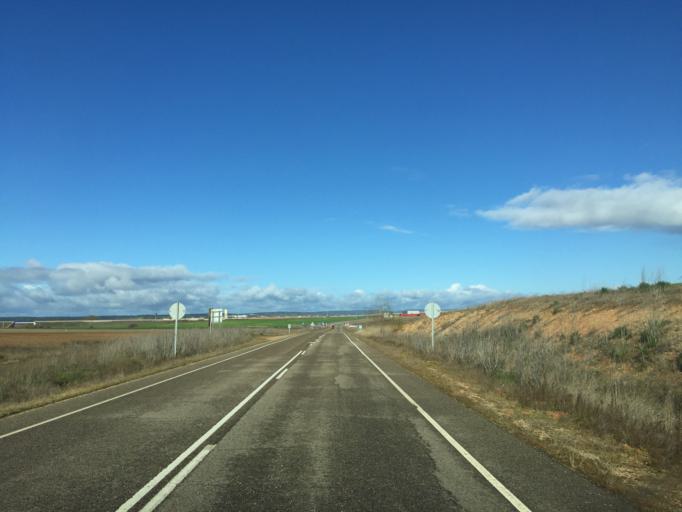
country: ES
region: Castille and Leon
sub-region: Provincia de Zamora
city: Manganeses de la Lampreana
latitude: 41.7602
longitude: -5.7444
